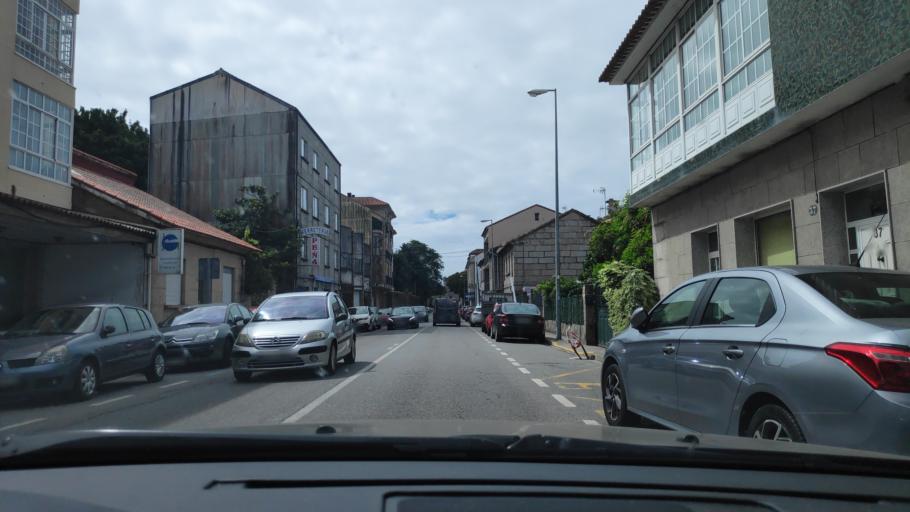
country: ES
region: Galicia
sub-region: Provincia de Pontevedra
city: Cambados
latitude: 42.5217
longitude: -8.8129
